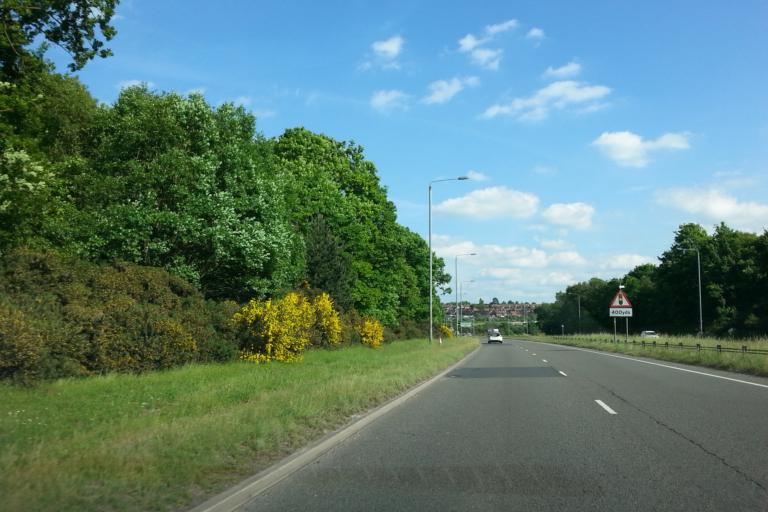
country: GB
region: England
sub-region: Nottinghamshire
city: Rainworth
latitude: 53.1250
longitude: -1.1221
